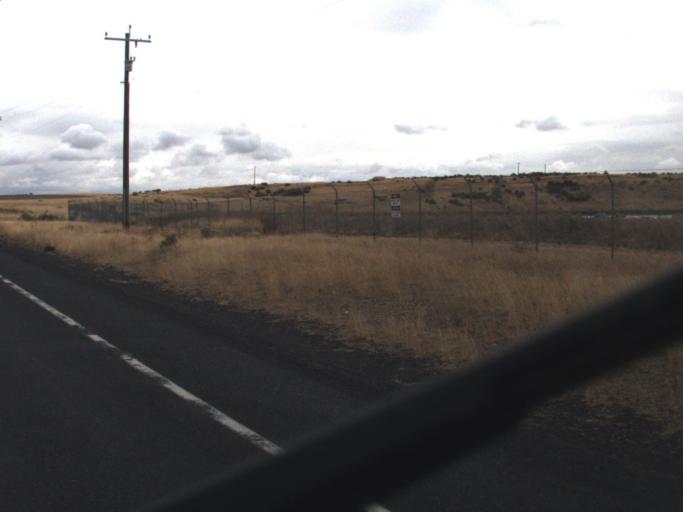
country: US
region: Washington
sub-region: Okanogan County
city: Coulee Dam
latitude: 47.7116
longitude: -118.9225
